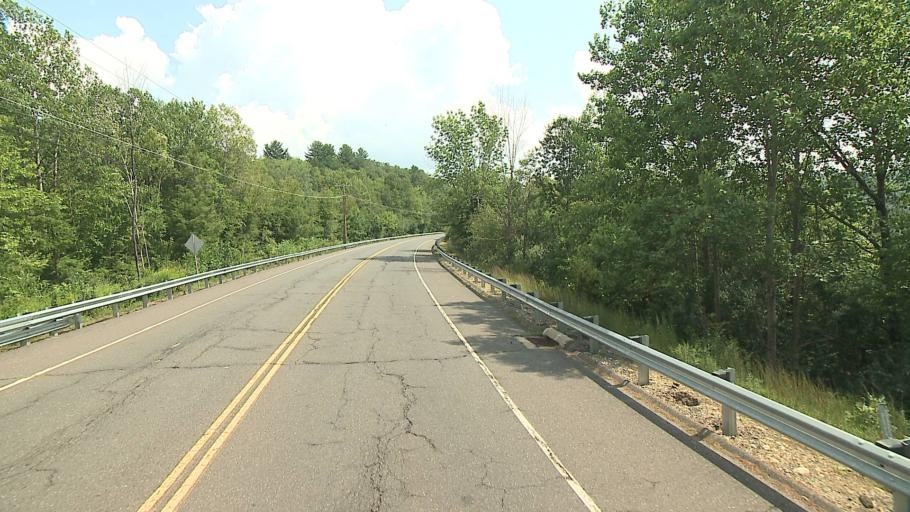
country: US
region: Connecticut
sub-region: Litchfield County
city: Thomaston
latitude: 41.6626
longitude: -73.1097
